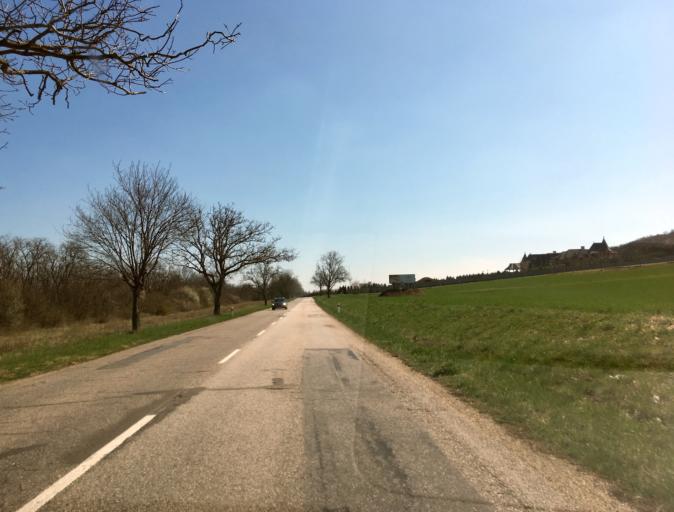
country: SK
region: Nitriansky
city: Svodin
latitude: 47.8602
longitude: 18.4838
